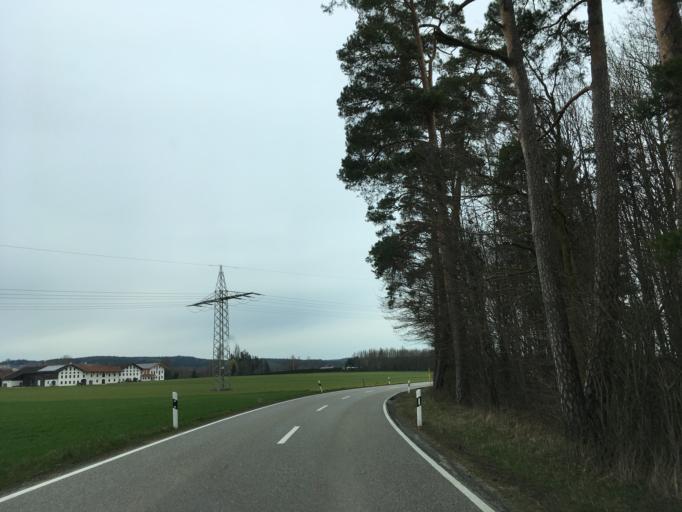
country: DE
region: Bavaria
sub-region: Upper Bavaria
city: Schnaitsee
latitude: 48.0927
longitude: 12.4080
